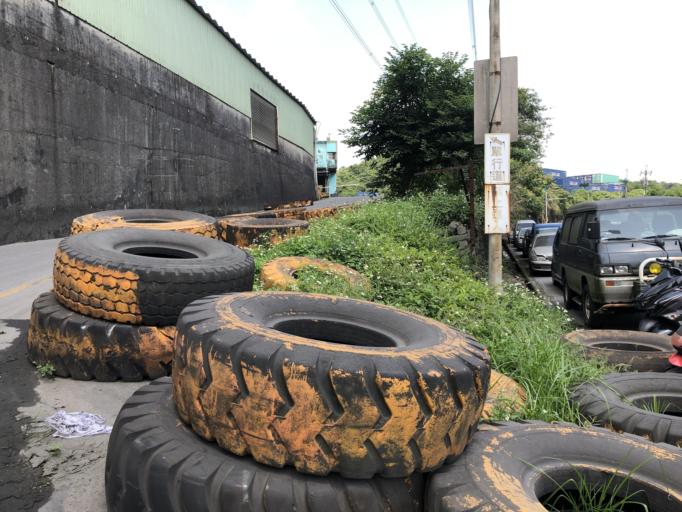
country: TW
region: Taiwan
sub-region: Keelung
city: Keelung
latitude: 25.0761
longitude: 121.6827
